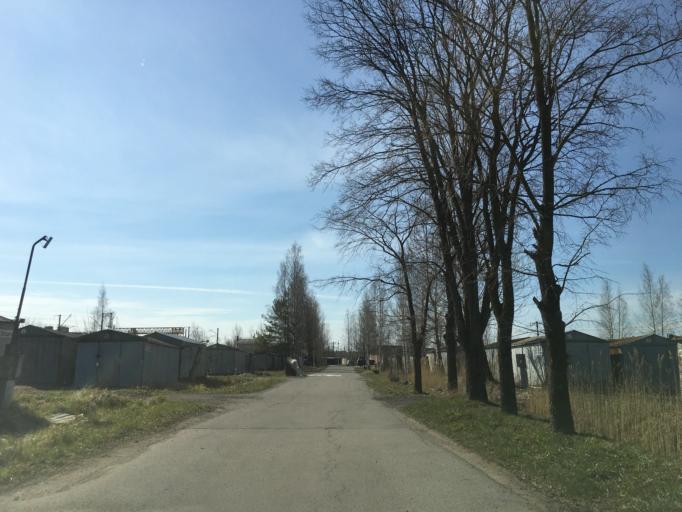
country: RU
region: St.-Petersburg
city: Uritsk
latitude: 59.8207
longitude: 30.1645
